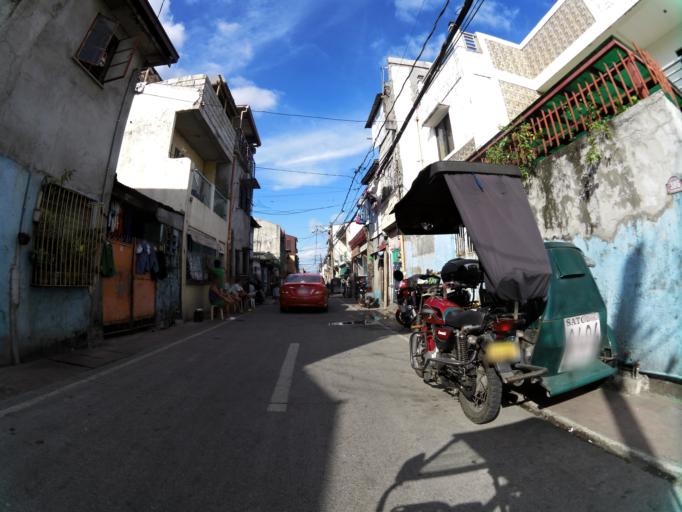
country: PH
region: Metro Manila
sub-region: Marikina
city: Calumpang
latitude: 14.6405
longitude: 121.0983
